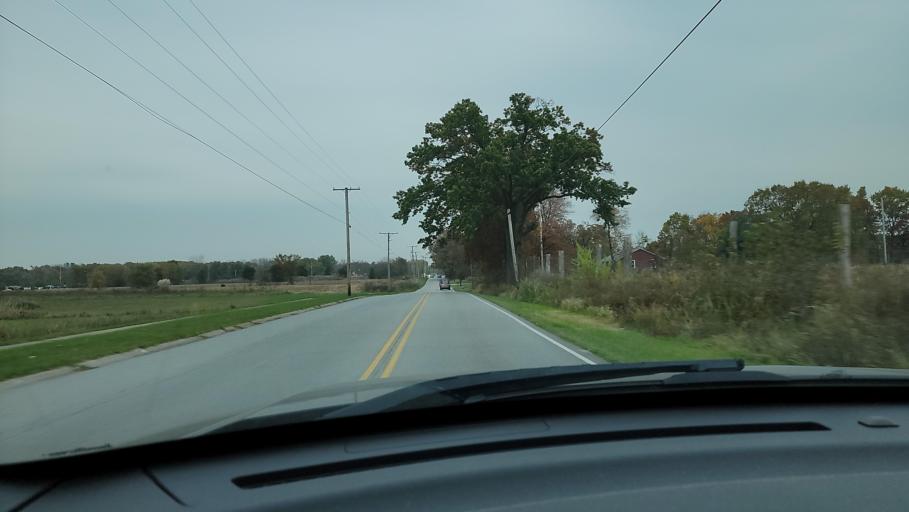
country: US
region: Indiana
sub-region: Lake County
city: Lake Station
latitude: 41.5552
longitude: -87.2216
